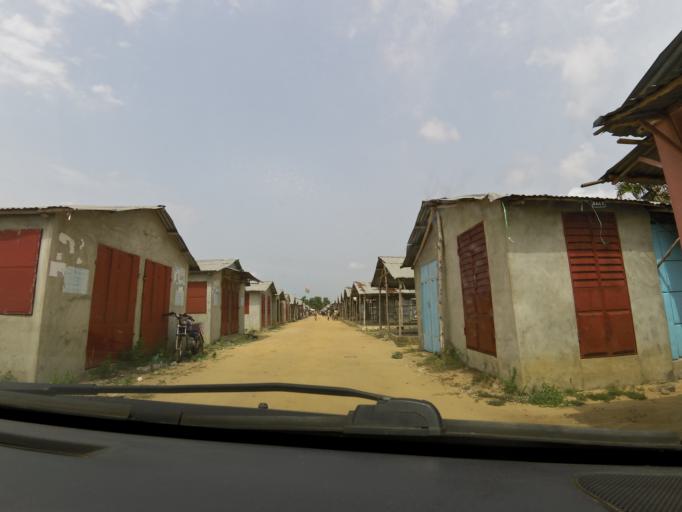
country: BJ
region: Queme
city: Porto-Novo
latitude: 6.3795
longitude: 2.6279
